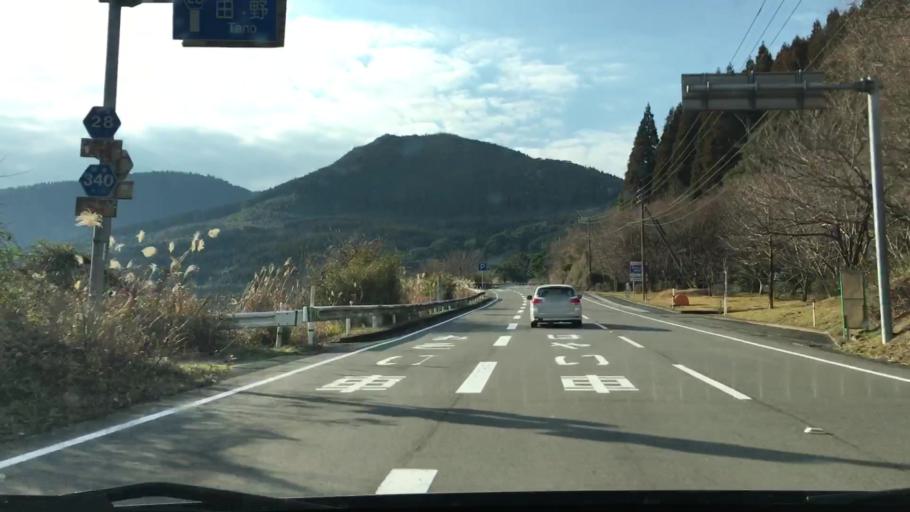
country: JP
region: Miyazaki
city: Miyazaki-shi
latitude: 31.7799
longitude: 131.3277
